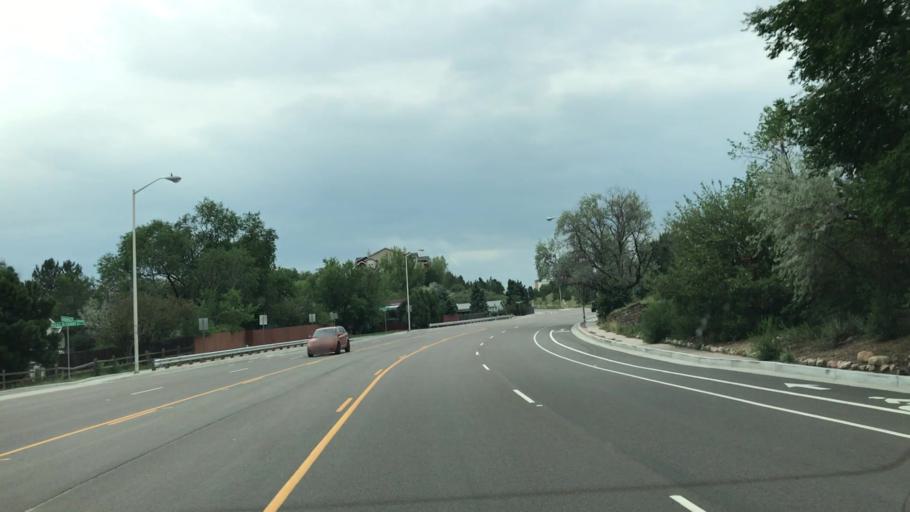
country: US
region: Colorado
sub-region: El Paso County
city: Colorado Springs
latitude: 38.8867
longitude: -104.8471
